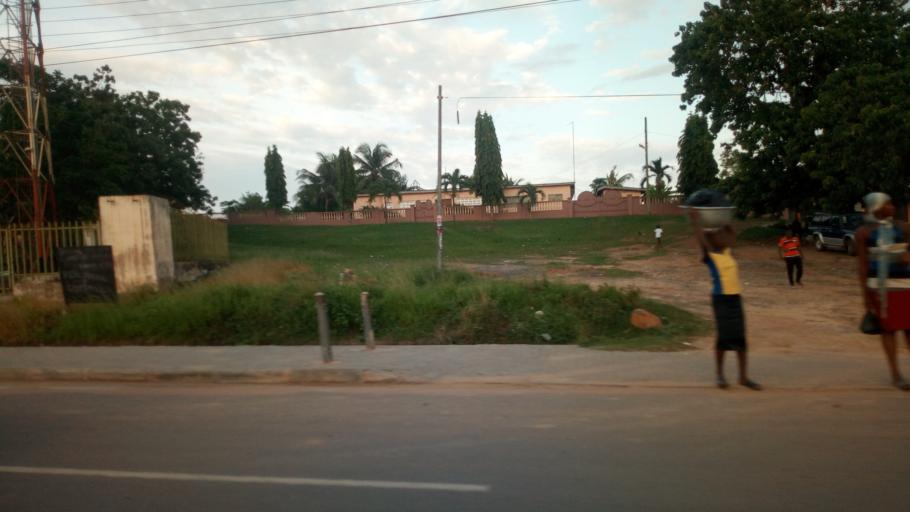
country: GH
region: Western
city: Takoradi
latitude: 4.9341
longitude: -1.7788
